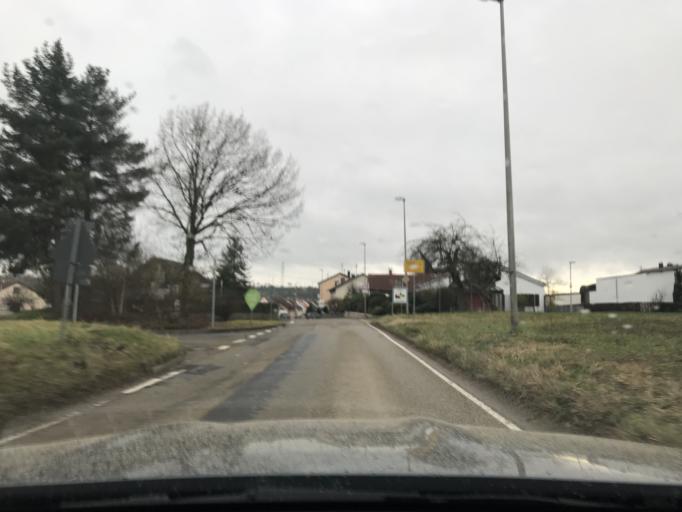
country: DE
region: Baden-Wuerttemberg
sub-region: Regierungsbezirk Stuttgart
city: Affalterbach
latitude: 48.9009
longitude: 9.2999
